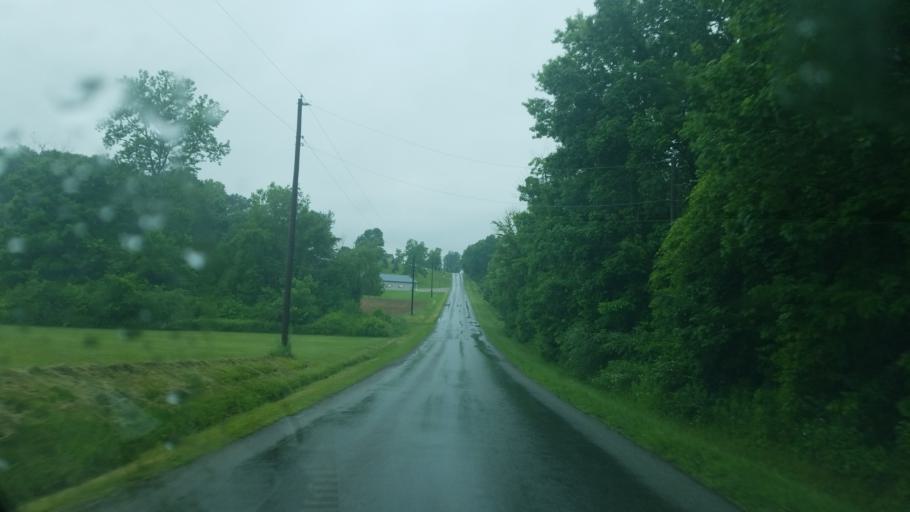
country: US
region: Ohio
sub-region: Huron County
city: Greenwich
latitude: 40.9385
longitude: -82.5578
